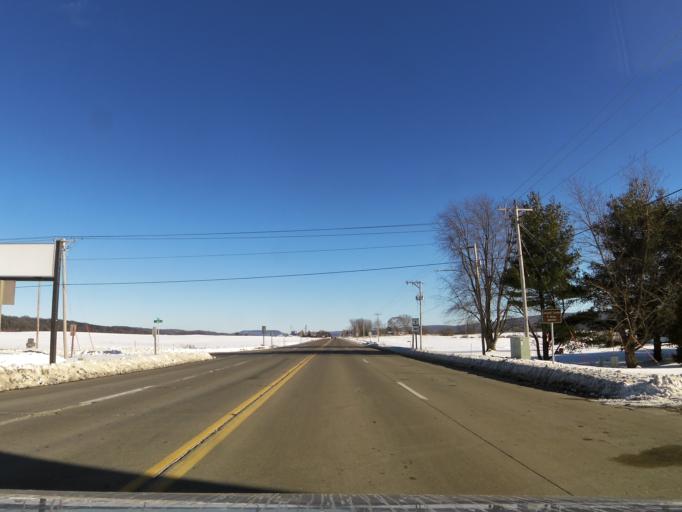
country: US
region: Wisconsin
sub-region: Sauk County
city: Baraboo
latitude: 43.4747
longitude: -89.7197
